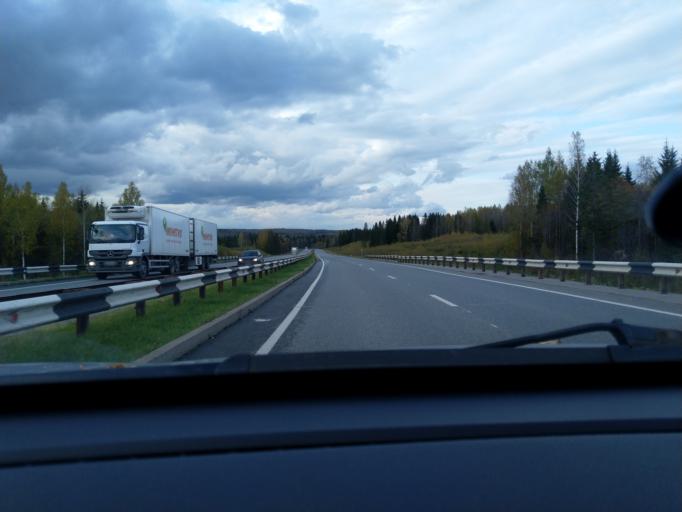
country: RU
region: Perm
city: Polazna
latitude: 58.3014
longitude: 56.4842
